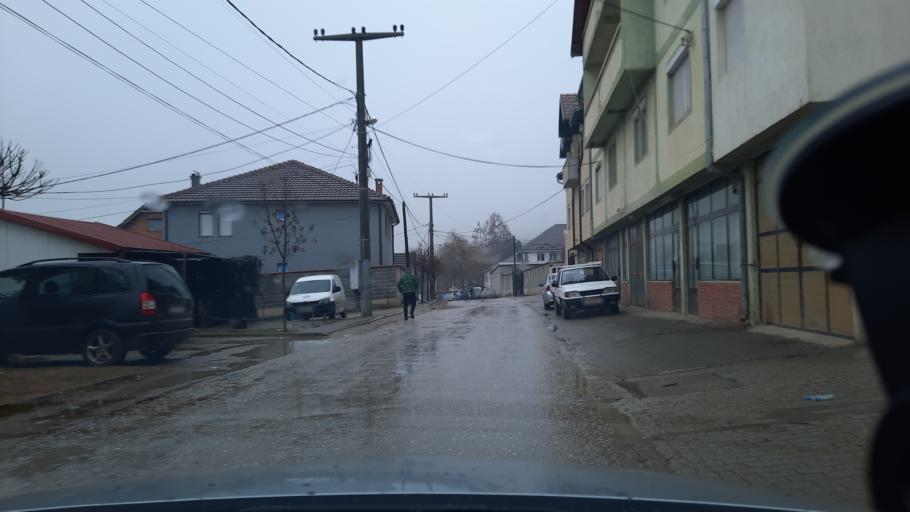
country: MK
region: Opstina Lipkovo
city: Lipkovo
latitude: 42.1551
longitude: 21.5861
